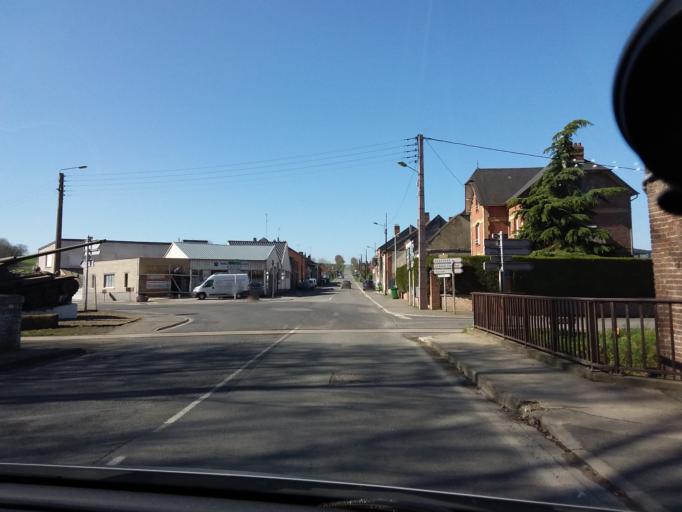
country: FR
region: Picardie
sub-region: Departement de l'Aisne
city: Montcornet
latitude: 49.6946
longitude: 4.0111
